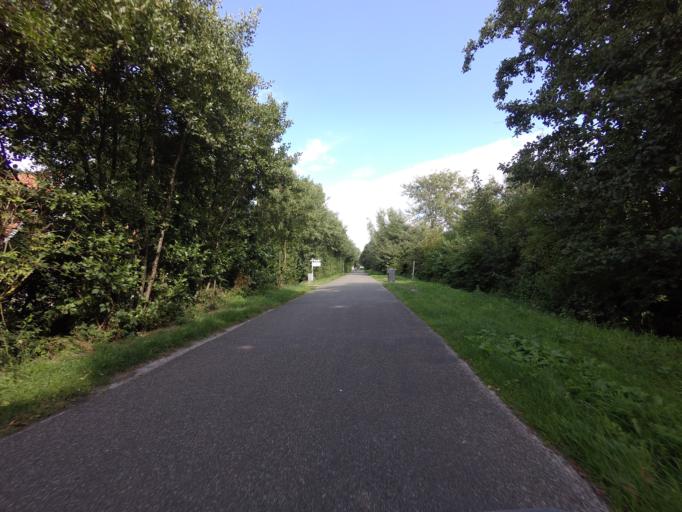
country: NL
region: Friesland
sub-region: Gemeente Terschelling
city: West-Terschelling
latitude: 53.3909
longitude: 5.2812
